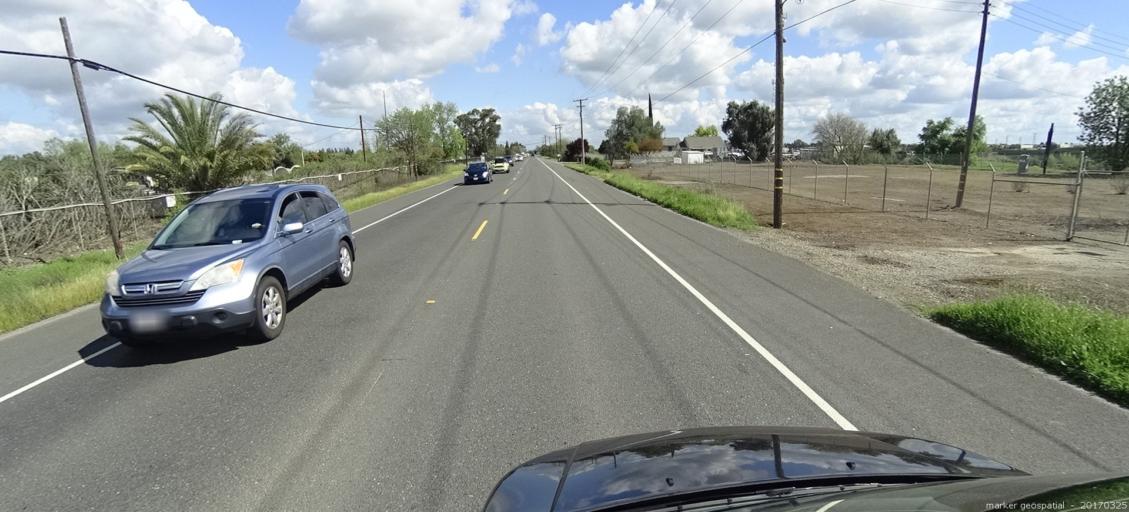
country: US
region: California
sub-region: Sacramento County
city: Rosemont
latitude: 38.5411
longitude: -121.3795
